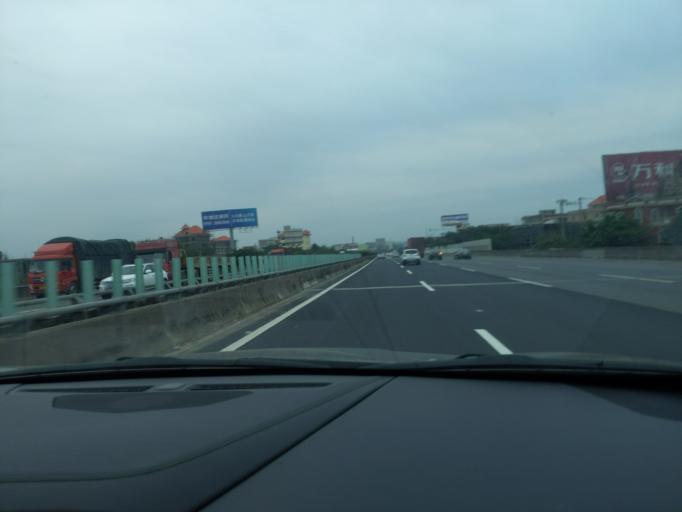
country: CN
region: Fujian
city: Anhai
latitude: 24.7371
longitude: 118.4226
